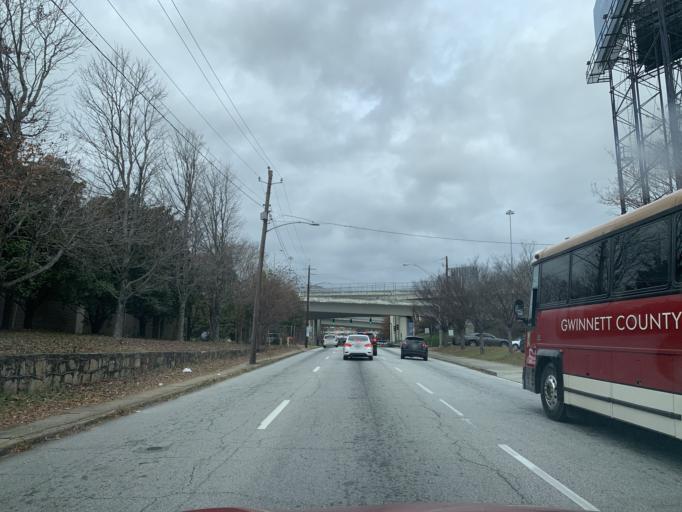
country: US
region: Georgia
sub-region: Fulton County
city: Atlanta
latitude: 33.7436
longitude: -84.3933
